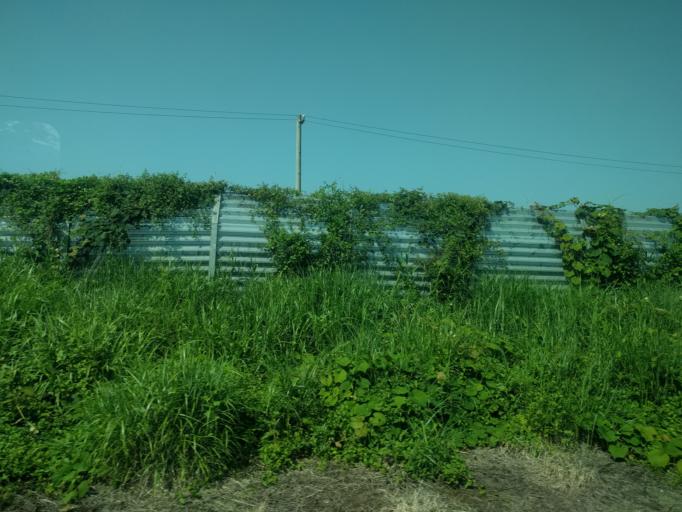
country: JP
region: Fukushima
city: Inawashiro
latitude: 37.5343
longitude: 140.1379
